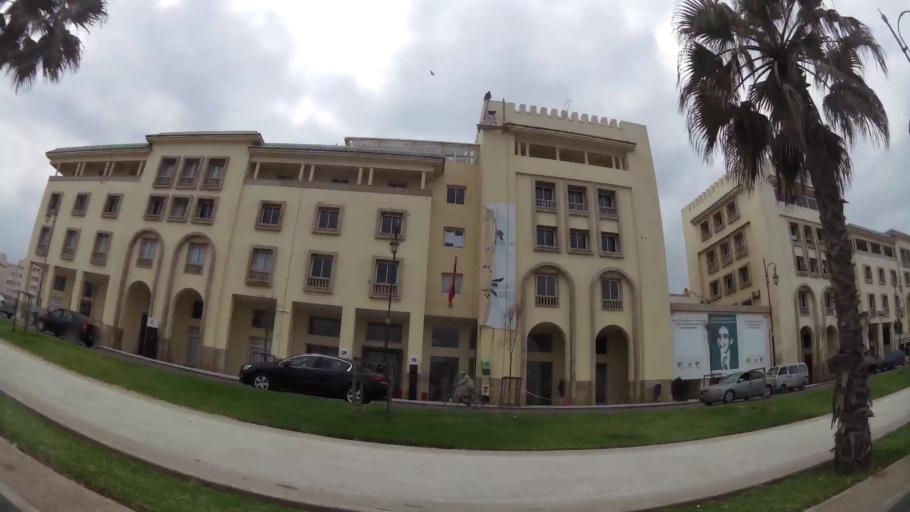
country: MA
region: Rabat-Sale-Zemmour-Zaer
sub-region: Rabat
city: Rabat
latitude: 33.9972
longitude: -6.8780
